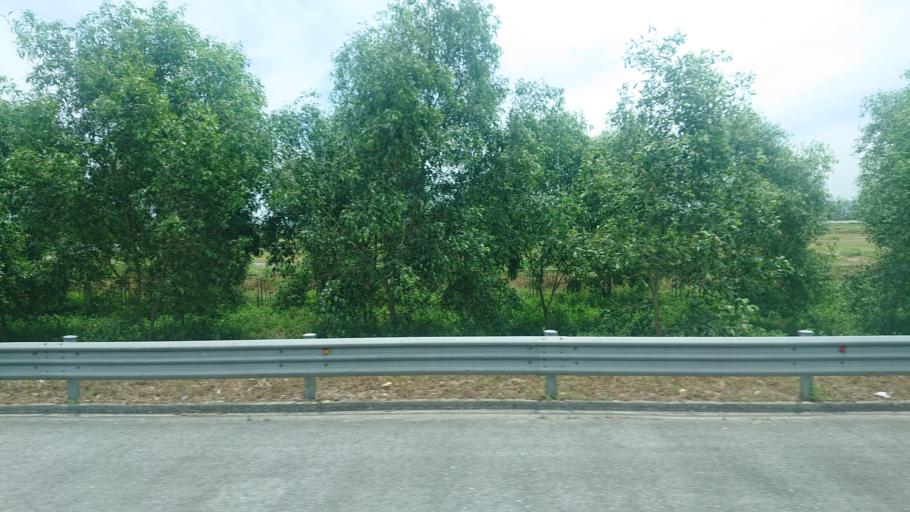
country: VN
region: Hai Phong
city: An Lao
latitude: 20.7981
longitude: 106.5396
